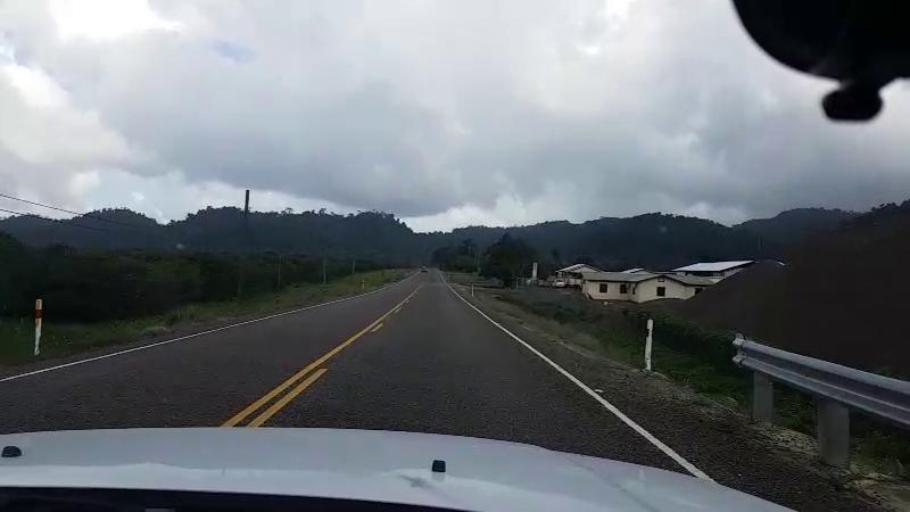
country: BZ
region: Cayo
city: Belmopan
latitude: 17.1485
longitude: -88.7083
